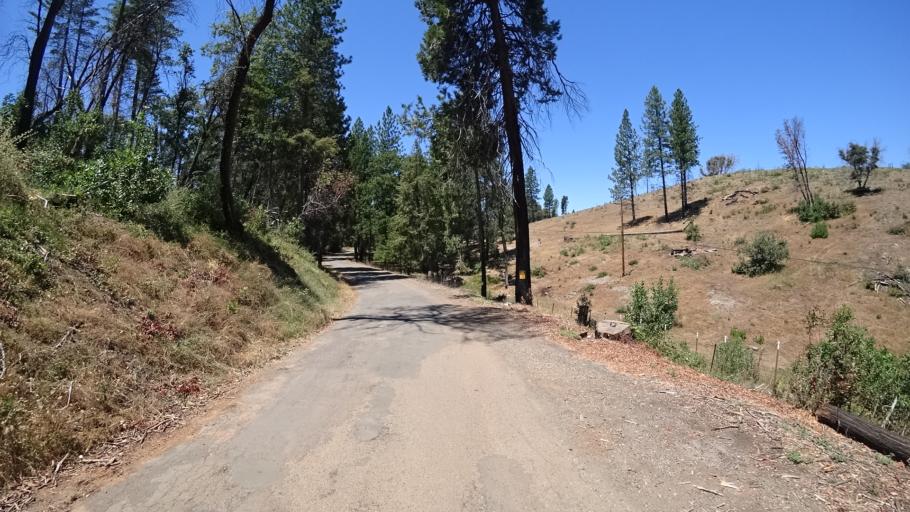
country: US
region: California
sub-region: Calaveras County
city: Mountain Ranch
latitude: 38.2446
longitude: -120.5794
